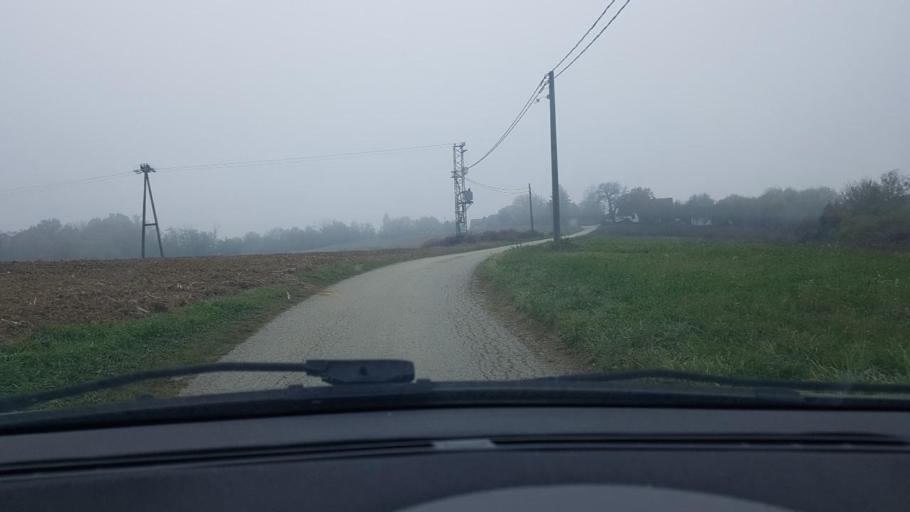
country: HR
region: Krapinsko-Zagorska
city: Zlatar
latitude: 46.1245
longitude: 16.1842
